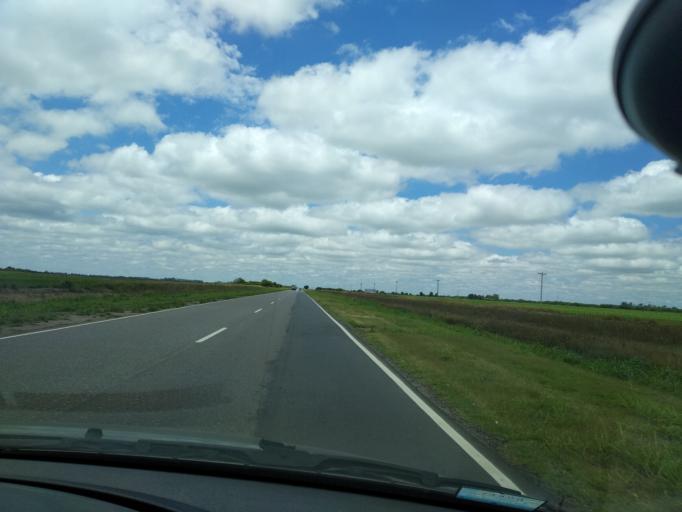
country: AR
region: Cordoba
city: Toledo
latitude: -31.6449
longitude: -64.0074
